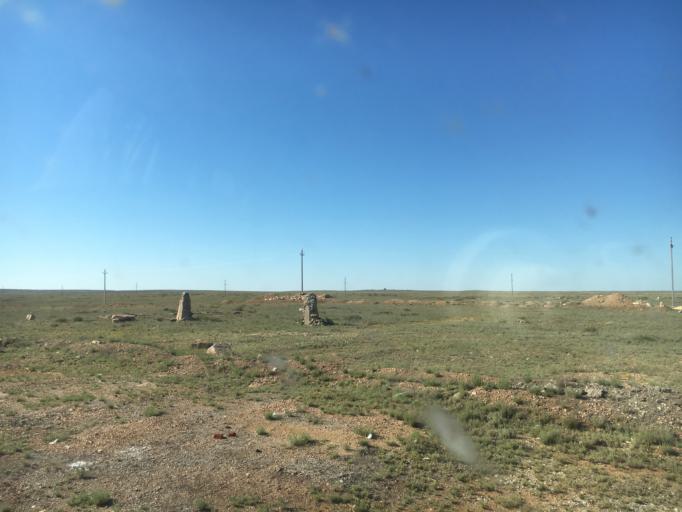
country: RU
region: Orenburg
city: Dombarovskiy
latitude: 50.0823
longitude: 59.5693
